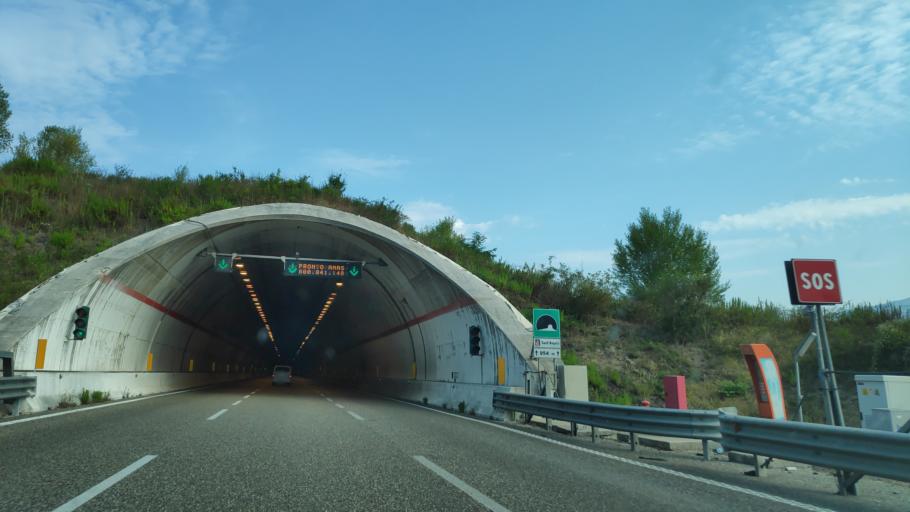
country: IT
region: Campania
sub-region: Provincia di Salerno
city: Contursi Terme
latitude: 40.6191
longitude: 15.2441
